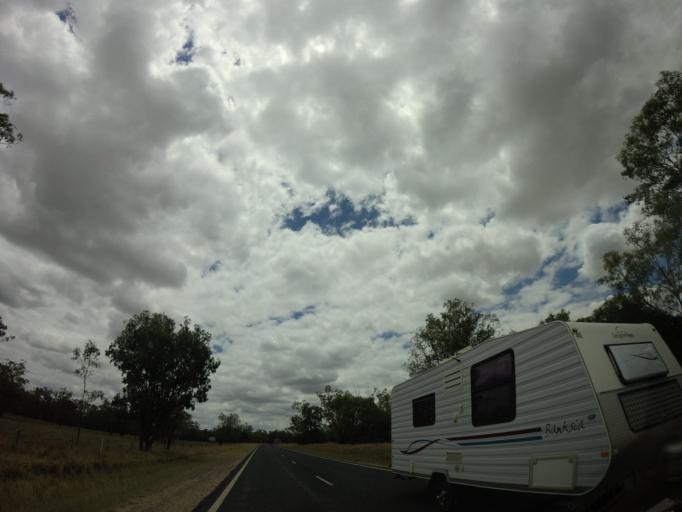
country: AU
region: Queensland
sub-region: Goondiwindi
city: Goondiwindi
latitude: -28.4688
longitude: 150.2931
